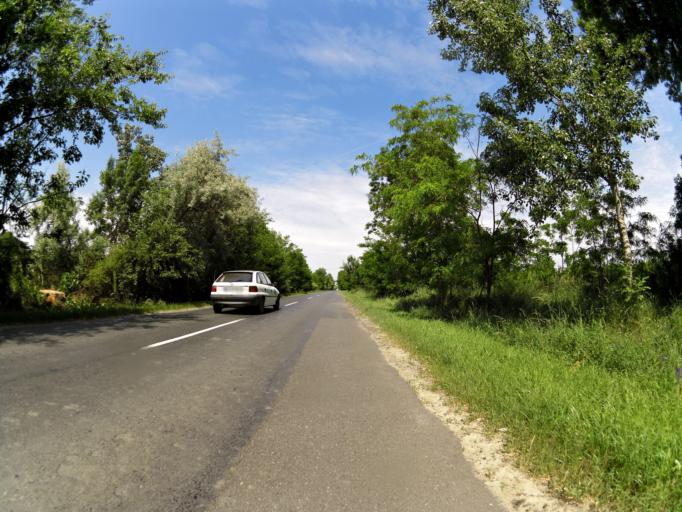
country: HU
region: Csongrad
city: Opusztaszer
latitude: 46.4713
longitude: 20.0907
